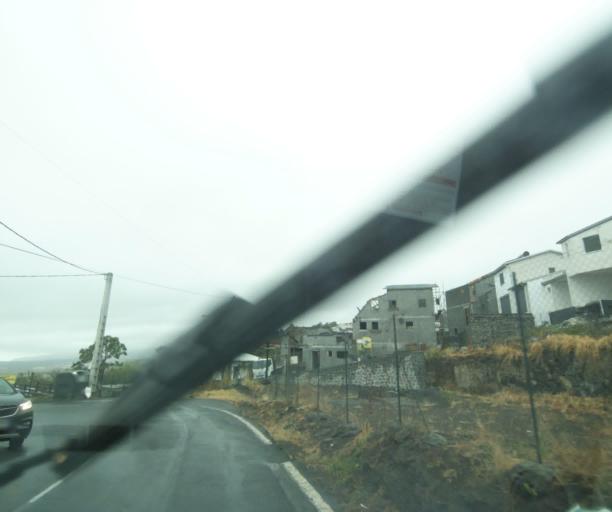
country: RE
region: Reunion
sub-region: Reunion
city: Saint-Paul
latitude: -21.0170
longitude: 55.2879
